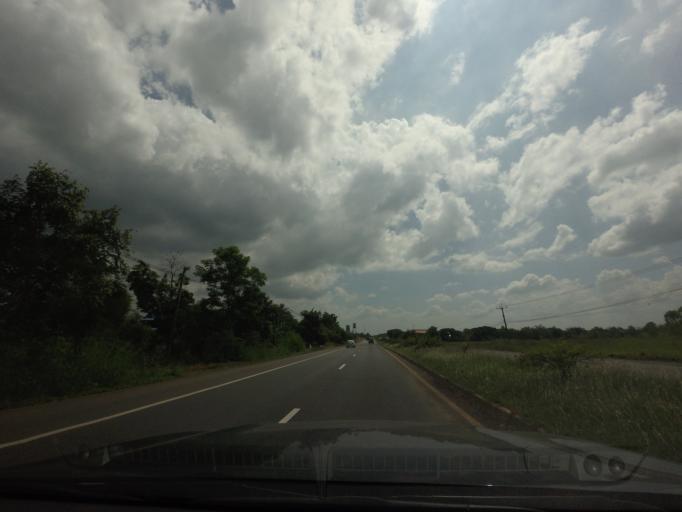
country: TH
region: Phetchabun
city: Nong Phai
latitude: 16.2082
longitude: 101.0890
